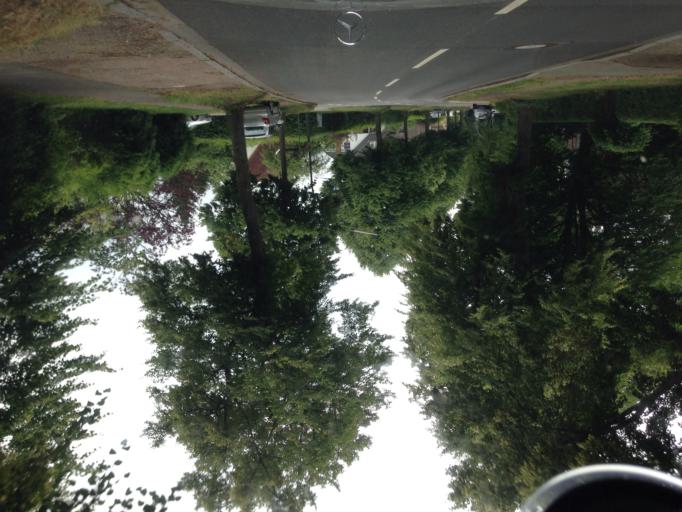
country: DE
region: Hamburg
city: Wandsbek
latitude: 53.5744
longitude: 10.1163
